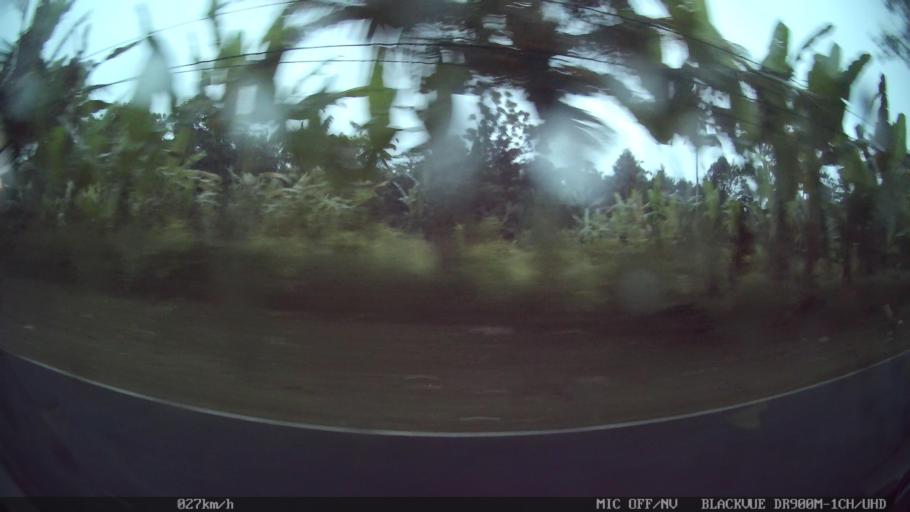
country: ID
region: Bali
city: Banjar Taro Kelod
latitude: -8.3637
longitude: 115.2710
